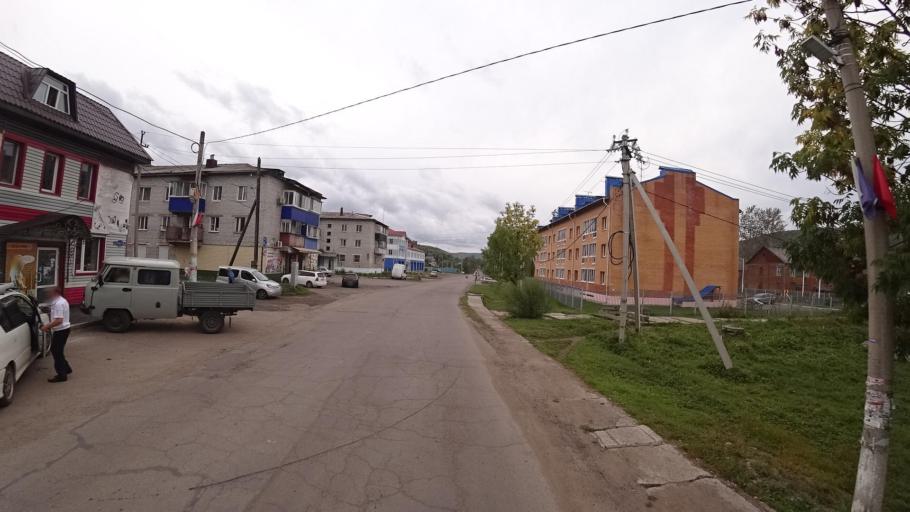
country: RU
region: Jewish Autonomous Oblast
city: Khingansk
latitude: 49.0096
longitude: 131.0574
